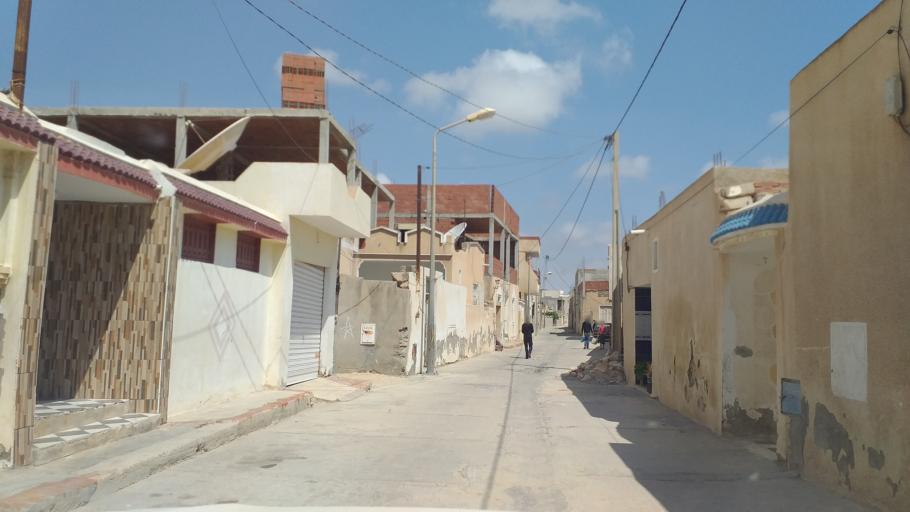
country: TN
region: Qabis
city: Gabes
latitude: 33.9425
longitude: 10.0648
